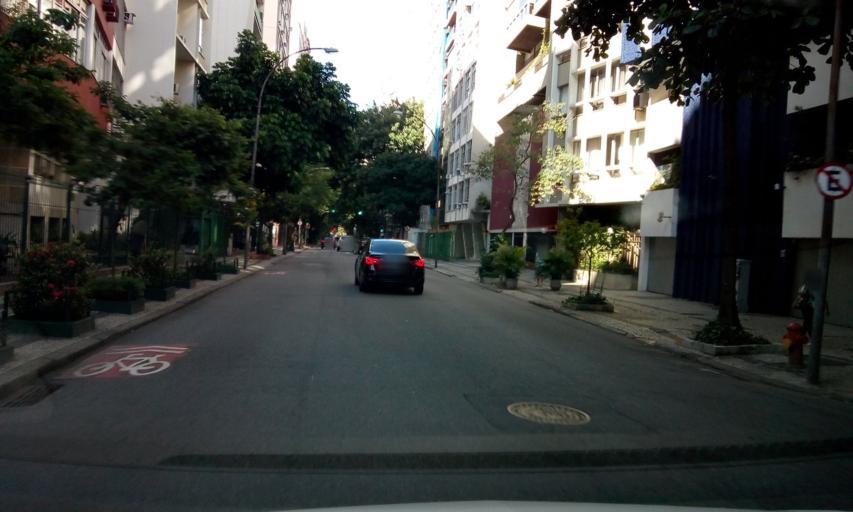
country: BR
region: Rio de Janeiro
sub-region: Rio De Janeiro
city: Rio de Janeiro
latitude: -22.9651
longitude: -43.1825
